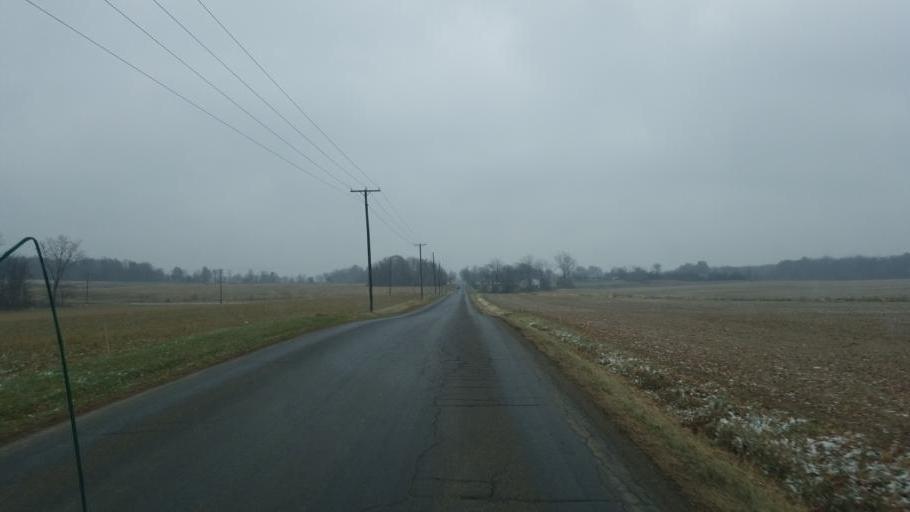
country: US
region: Ohio
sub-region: Huron County
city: Greenwich
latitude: 40.9753
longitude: -82.5631
